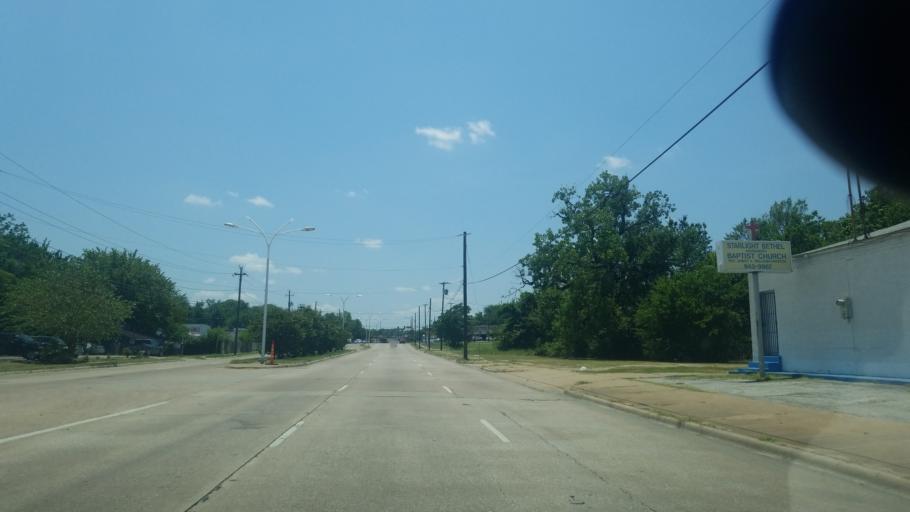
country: US
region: Texas
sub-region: Dallas County
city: Dallas
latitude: 32.7447
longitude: -96.7873
